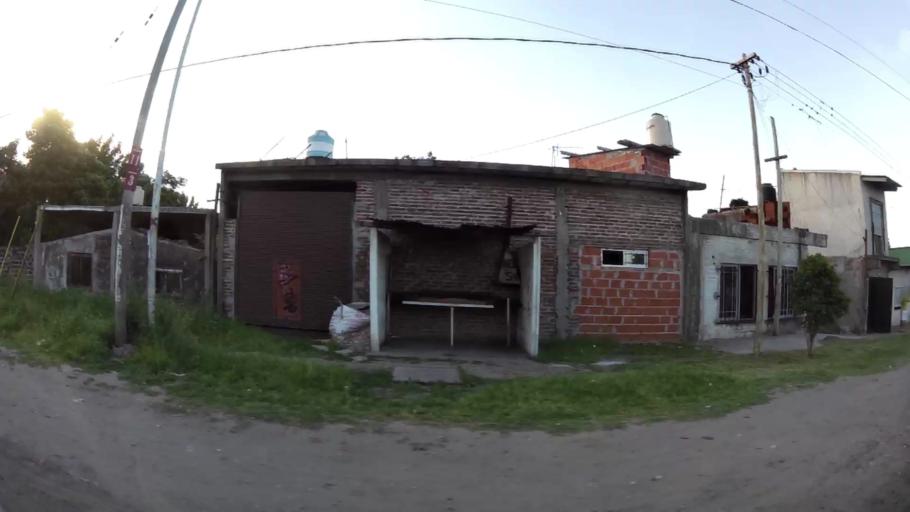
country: AR
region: Buenos Aires
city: Ituzaingo
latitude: -34.6949
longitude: -58.6401
